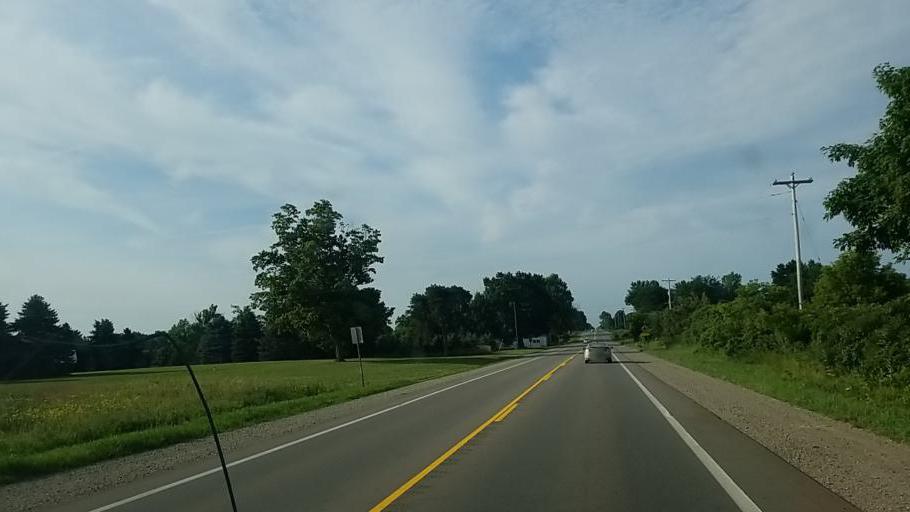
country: US
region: Michigan
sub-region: Ionia County
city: Ionia
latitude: 42.9038
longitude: -85.0749
